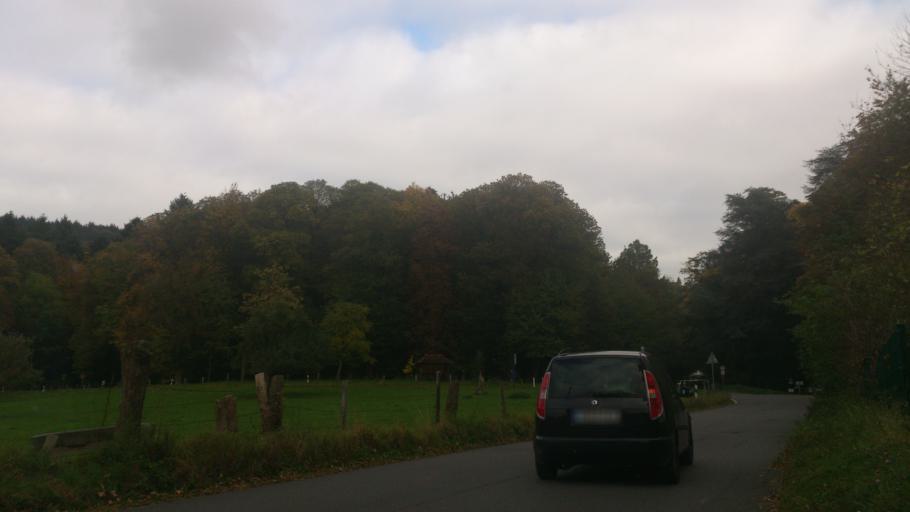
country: DE
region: Baden-Wuerttemberg
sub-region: Karlsruhe Region
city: Heidelberg
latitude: 49.3904
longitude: 8.7039
